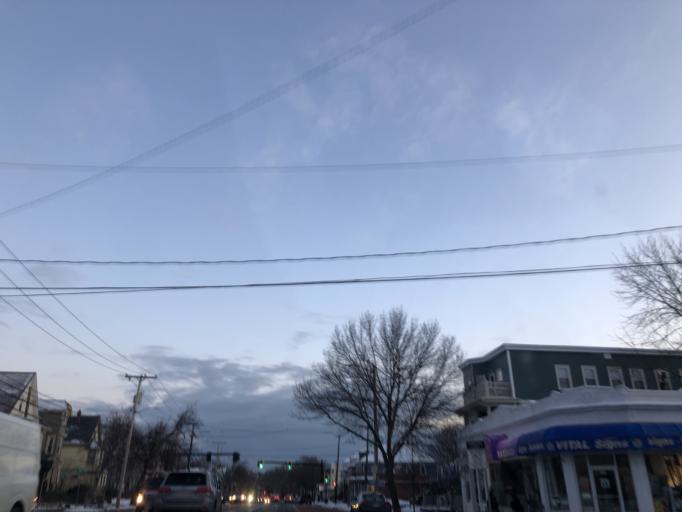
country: US
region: Massachusetts
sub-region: Middlesex County
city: Arlington
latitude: 42.4034
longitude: -71.1393
